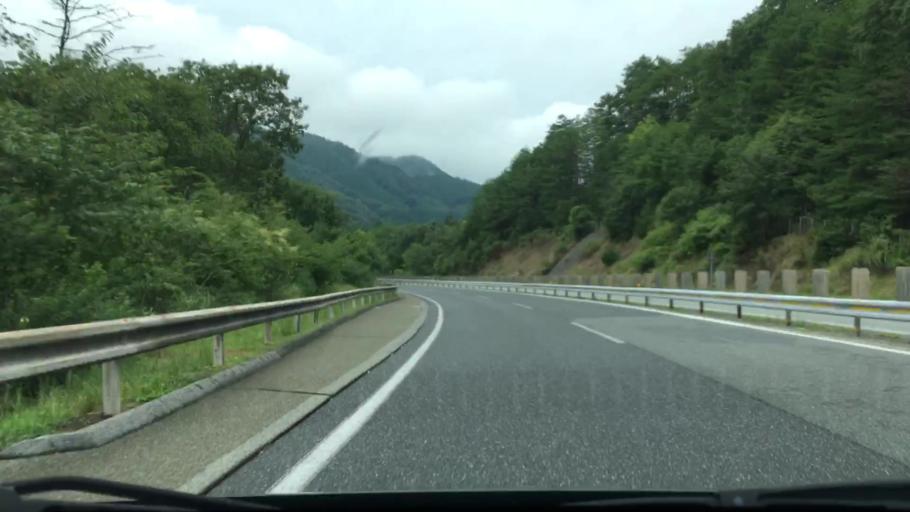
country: JP
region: Hiroshima
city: Shobara
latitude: 34.8599
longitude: 133.1013
